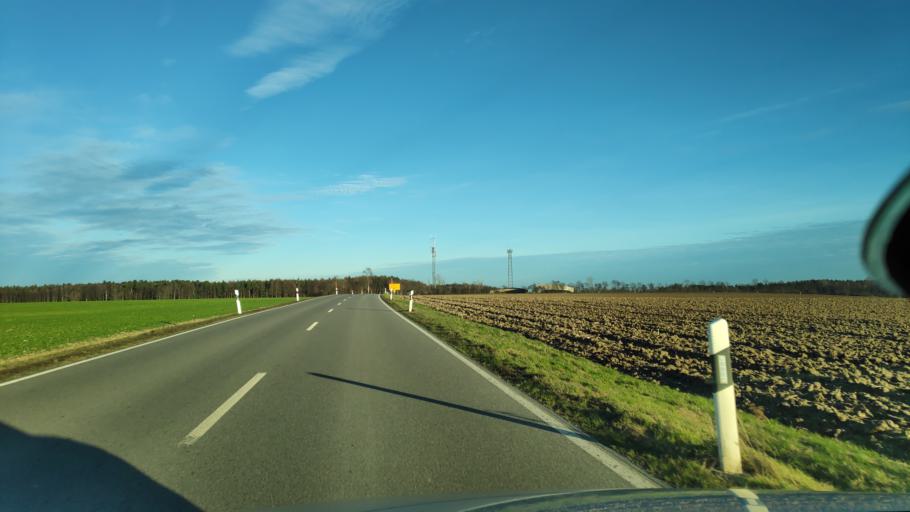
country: DE
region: Thuringia
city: Heukewalde
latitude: 50.8051
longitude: 12.2797
